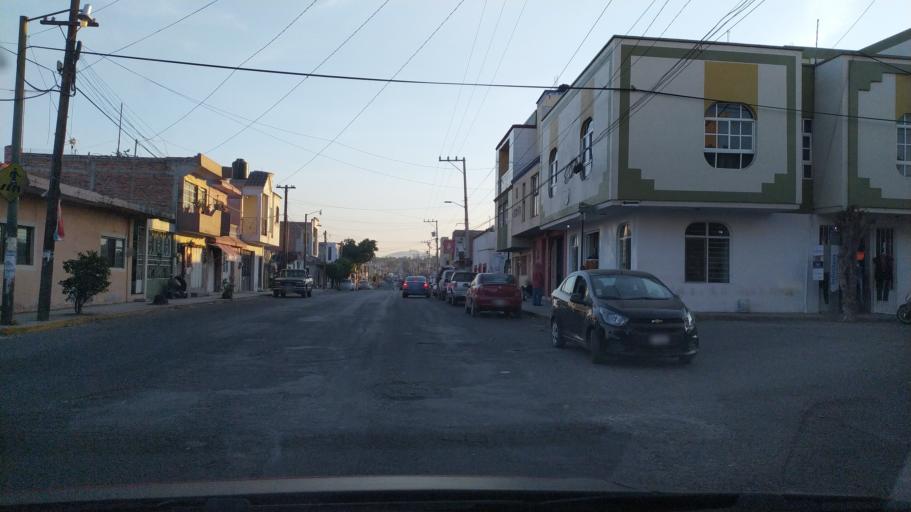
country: MX
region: Michoacan
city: Vistahermosa de Negrete
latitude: 20.2713
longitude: -102.4739
